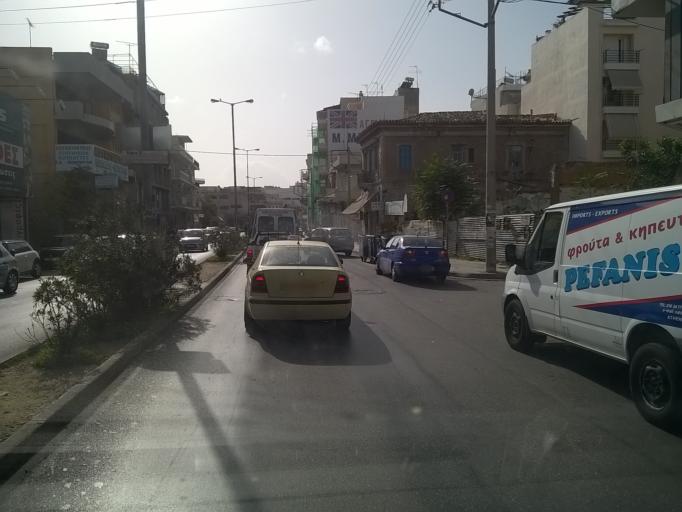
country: GR
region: Attica
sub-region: Nomos Piraios
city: Agios Ioannis Rentis
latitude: 37.9624
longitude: 23.6573
